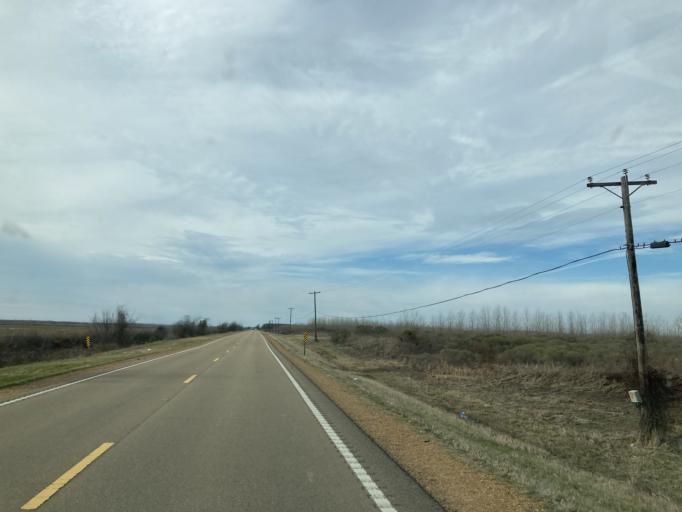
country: US
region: Mississippi
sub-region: Humphreys County
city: Belzoni
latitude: 33.1832
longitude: -90.6083
